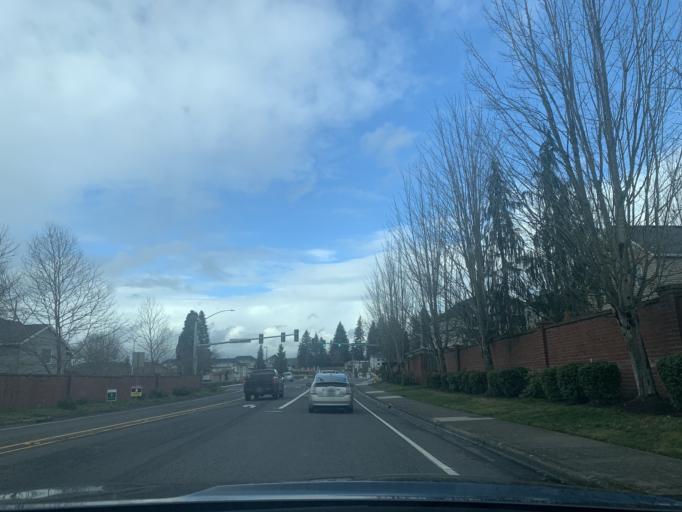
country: US
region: Oregon
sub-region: Washington County
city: Oak Hills
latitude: 45.5657
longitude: -122.8358
